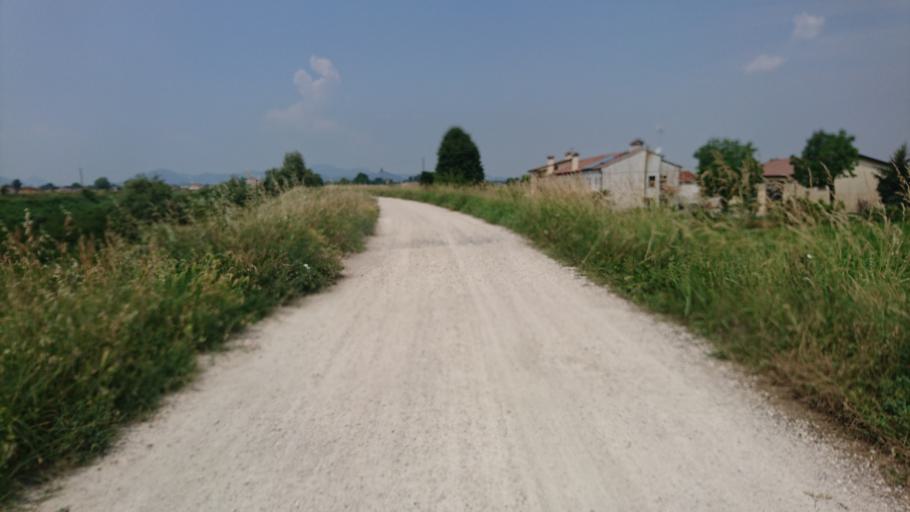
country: IT
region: Veneto
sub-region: Provincia di Padova
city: Cartura
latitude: 45.2816
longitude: 11.8882
